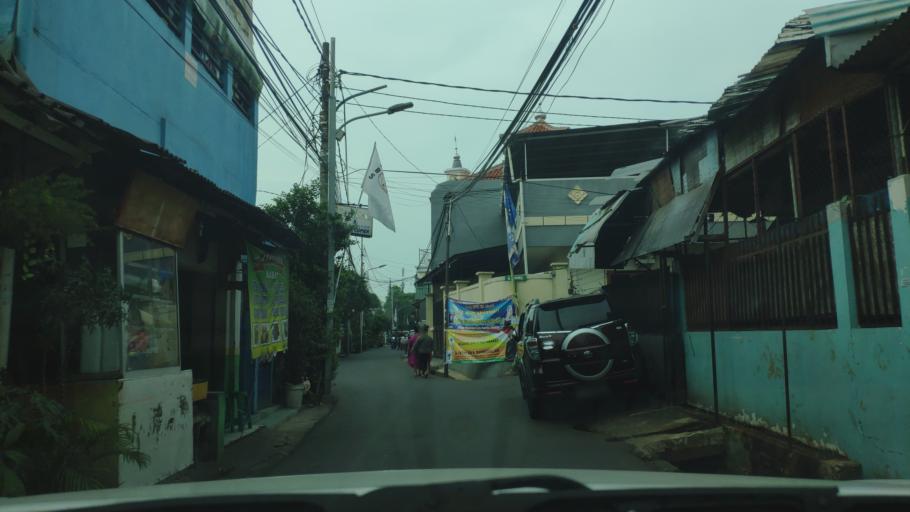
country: ID
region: Jakarta Raya
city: Jakarta
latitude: -6.1874
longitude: 106.8015
